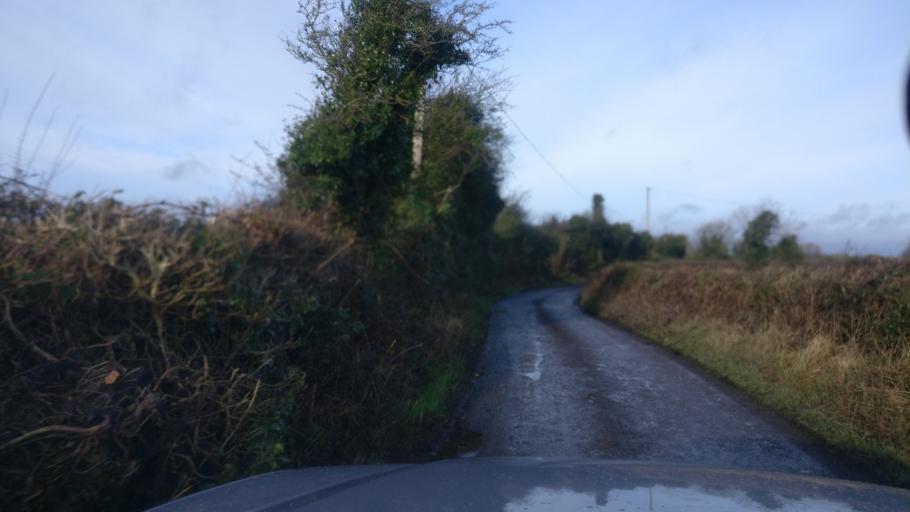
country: IE
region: Connaught
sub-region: County Galway
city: Loughrea
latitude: 53.2047
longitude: -8.6742
